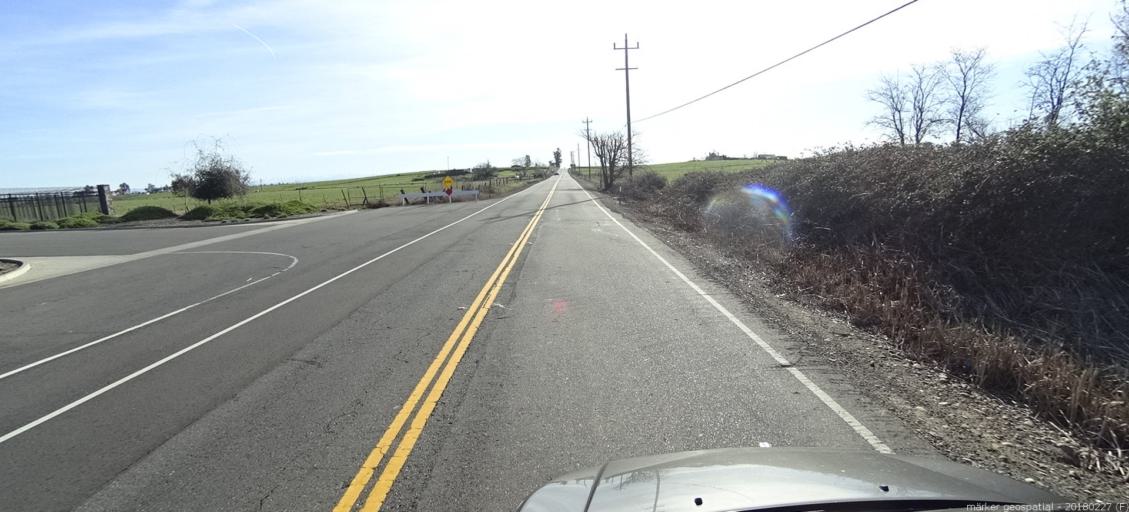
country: US
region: California
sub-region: Sacramento County
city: Vineyard
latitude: 38.4964
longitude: -121.3121
